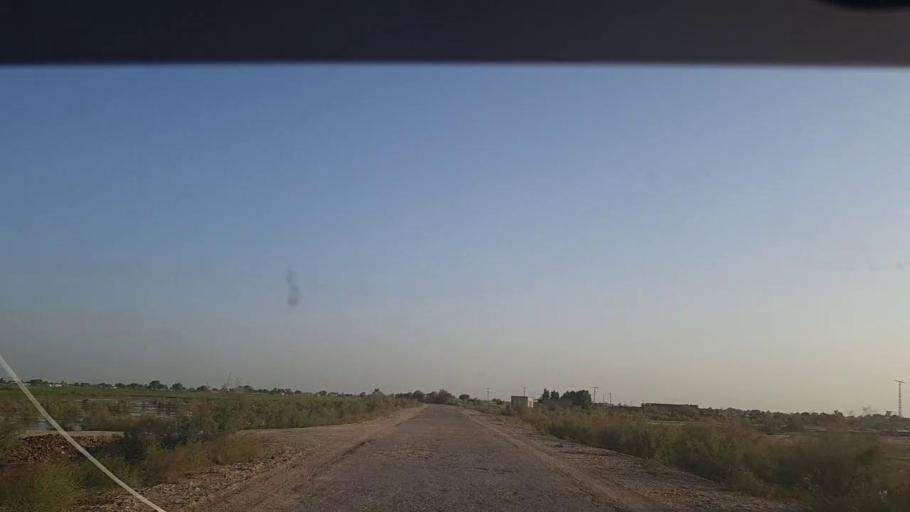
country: PK
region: Sindh
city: Thul
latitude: 28.1404
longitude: 68.8872
